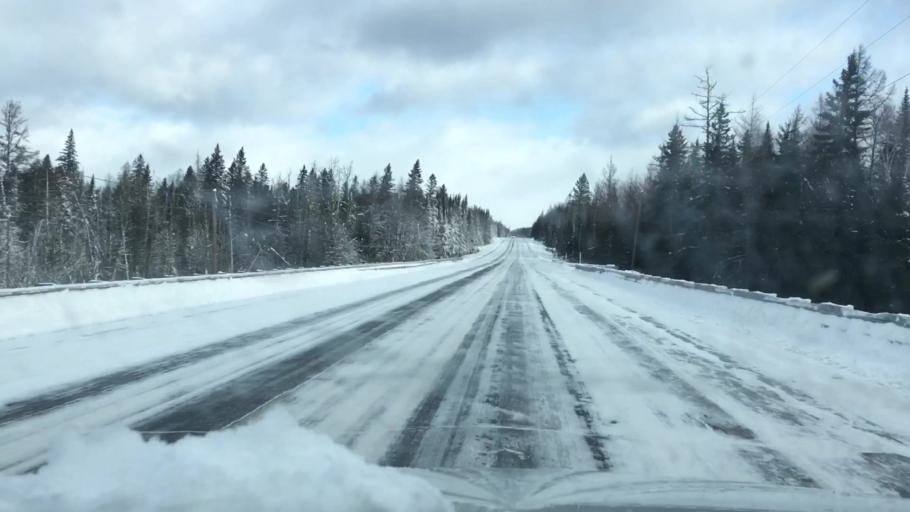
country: US
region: Maine
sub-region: Aroostook County
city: Madawaska
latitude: 47.0209
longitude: -68.0137
